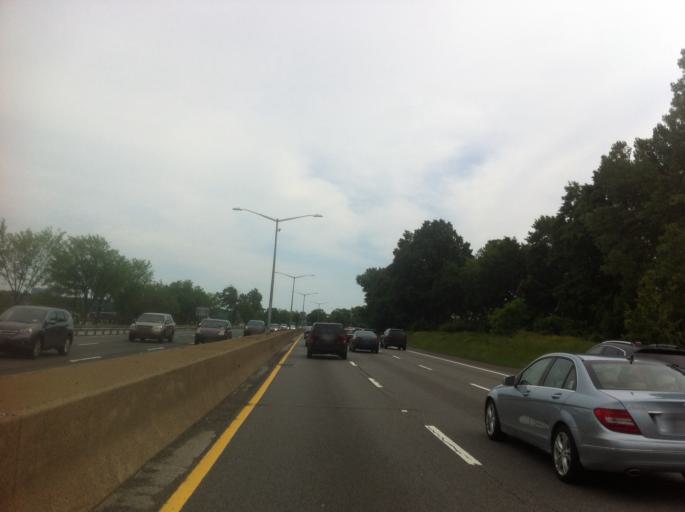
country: US
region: New York
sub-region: Nassau County
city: East Atlantic Beach
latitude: 40.7822
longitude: -73.7713
